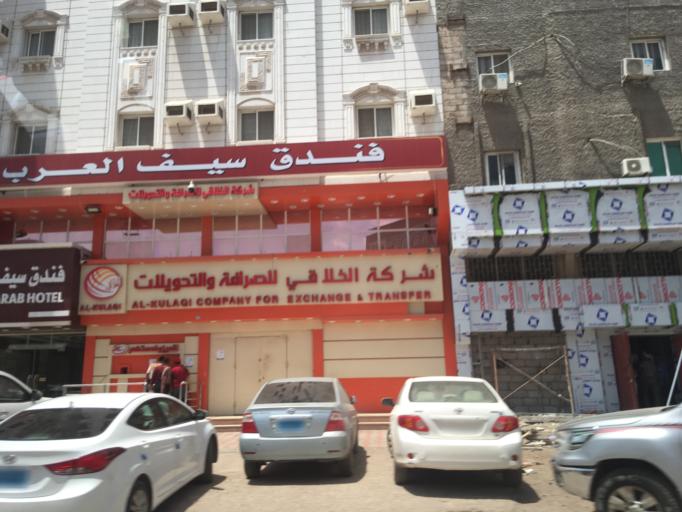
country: YE
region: Aden
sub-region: Al Mansura
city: Al Mansurah
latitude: 12.8643
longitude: 44.9712
